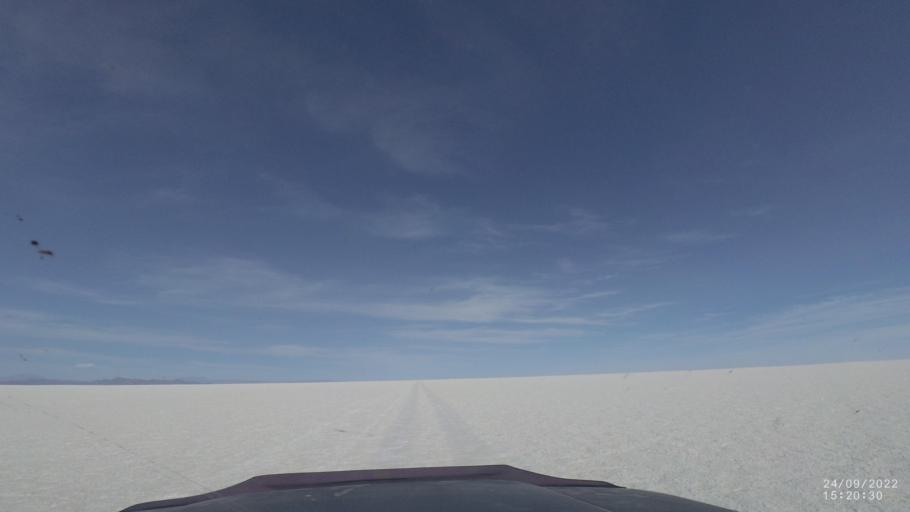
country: BO
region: Potosi
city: Colchani
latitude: -20.0129
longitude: -67.3985
